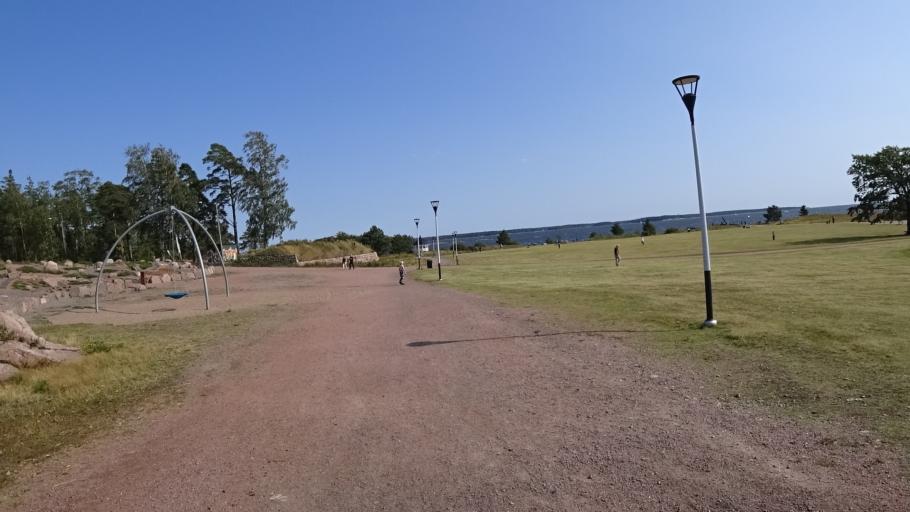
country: FI
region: Kymenlaakso
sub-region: Kotka-Hamina
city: Kotka
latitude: 60.4475
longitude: 26.9398
